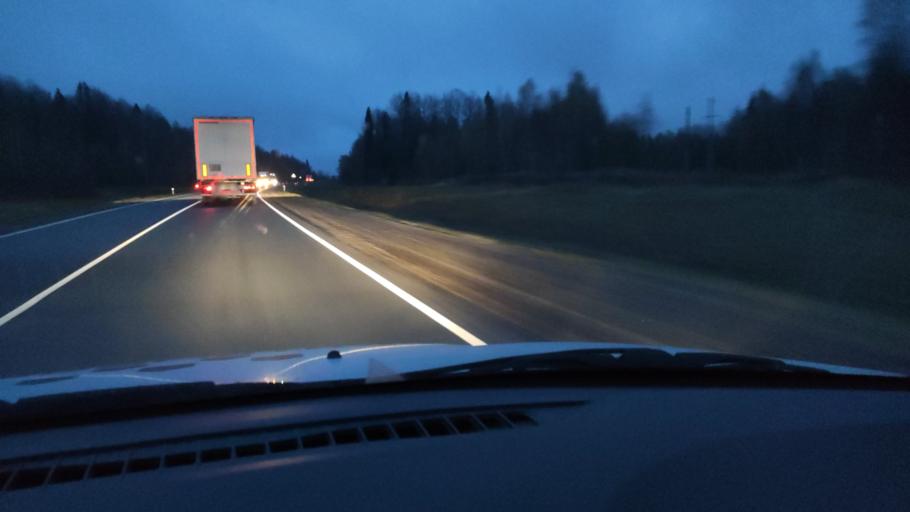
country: RU
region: Kirov
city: Kostino
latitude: 58.8156
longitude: 53.5836
